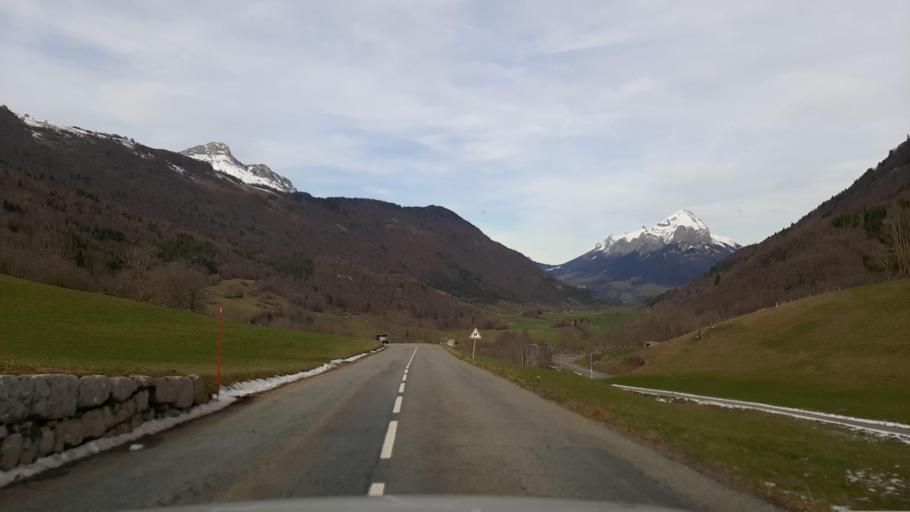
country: FR
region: Rhone-Alpes
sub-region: Departement de la Savoie
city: Coise-Saint-Jean-Pied-Gauthier
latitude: 45.5920
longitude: 6.1377
